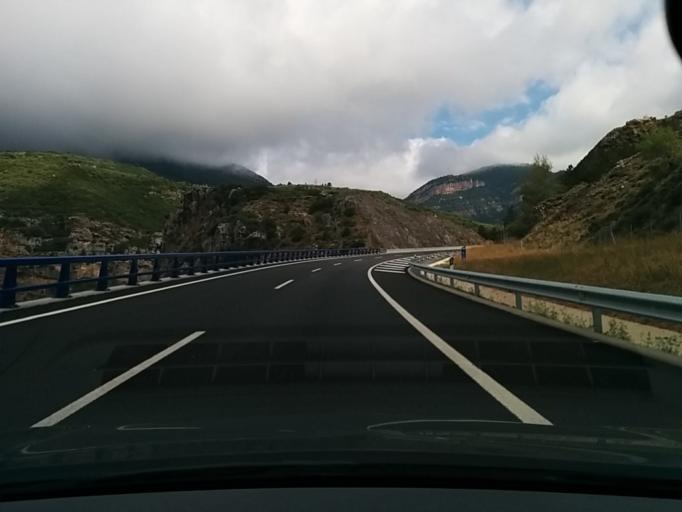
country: ES
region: Aragon
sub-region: Provincia de Huesca
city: Nueno
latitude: 42.2729
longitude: -0.4308
